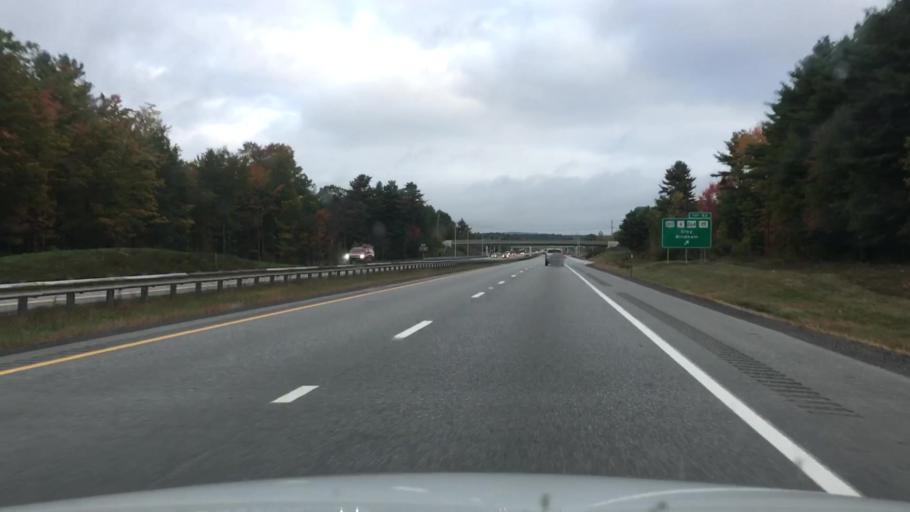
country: US
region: Maine
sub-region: Cumberland County
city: New Gloucester
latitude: 43.8757
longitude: -70.3313
